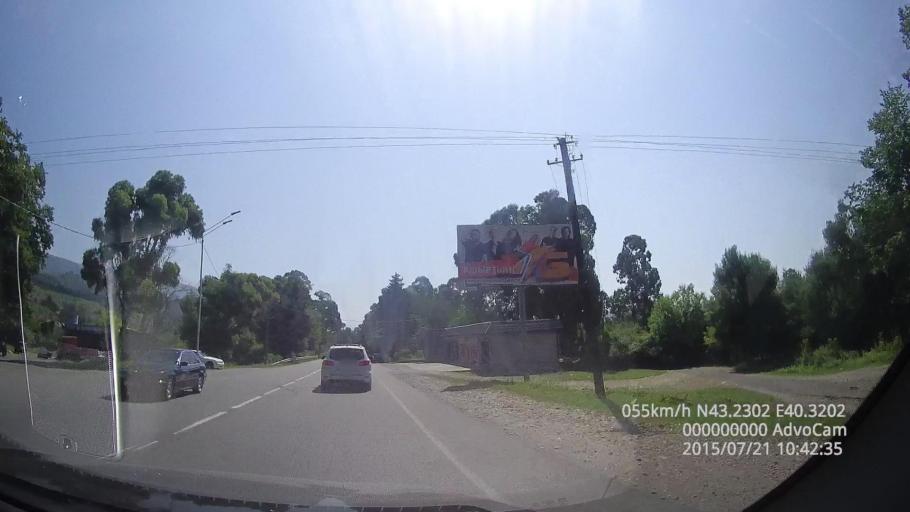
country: GE
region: Abkhazia
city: Gagra
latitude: 43.2302
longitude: 40.3208
